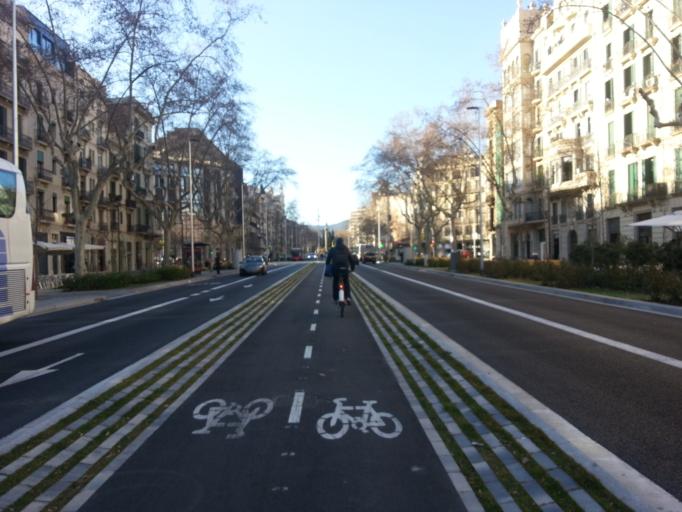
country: ES
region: Catalonia
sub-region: Provincia de Barcelona
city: Eixample
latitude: 41.3967
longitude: 2.1730
